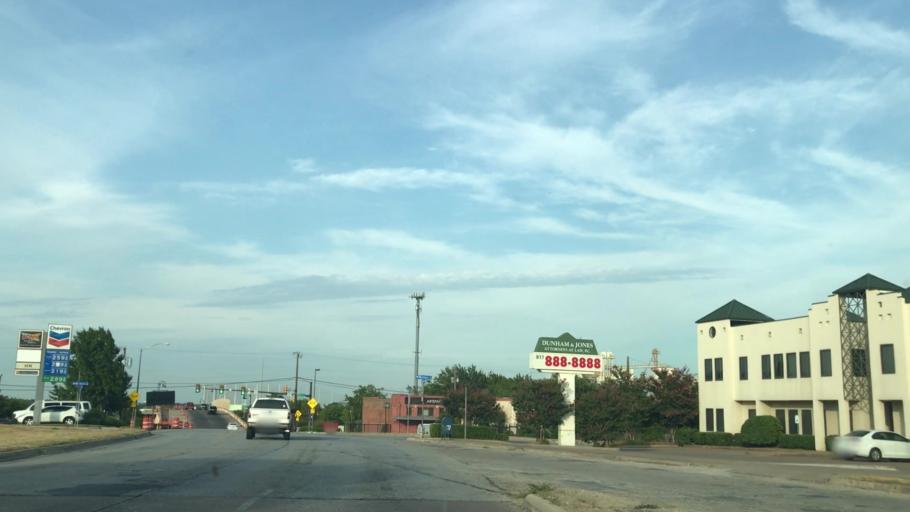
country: US
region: Texas
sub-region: Tarrant County
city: Fort Worth
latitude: 32.7609
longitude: -97.3253
